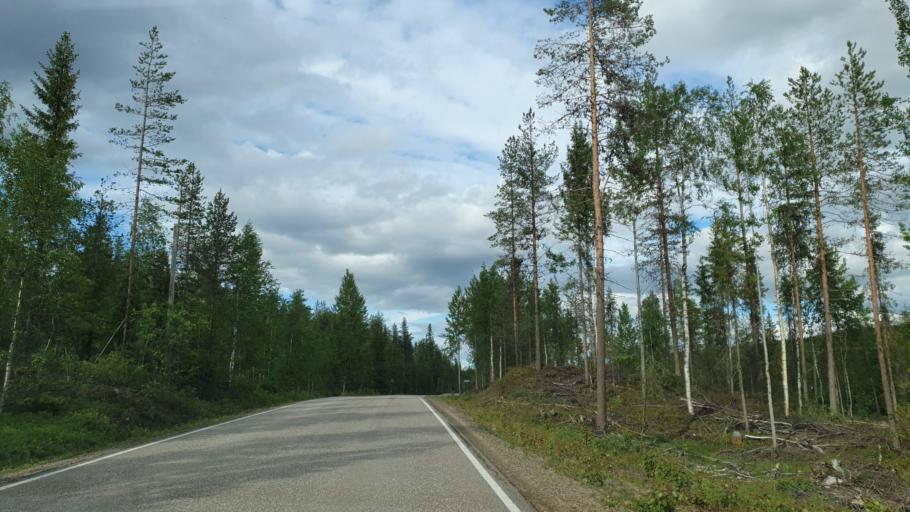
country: FI
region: Lapland
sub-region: Tunturi-Lappi
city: Kolari
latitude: 67.5783
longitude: 24.0718
